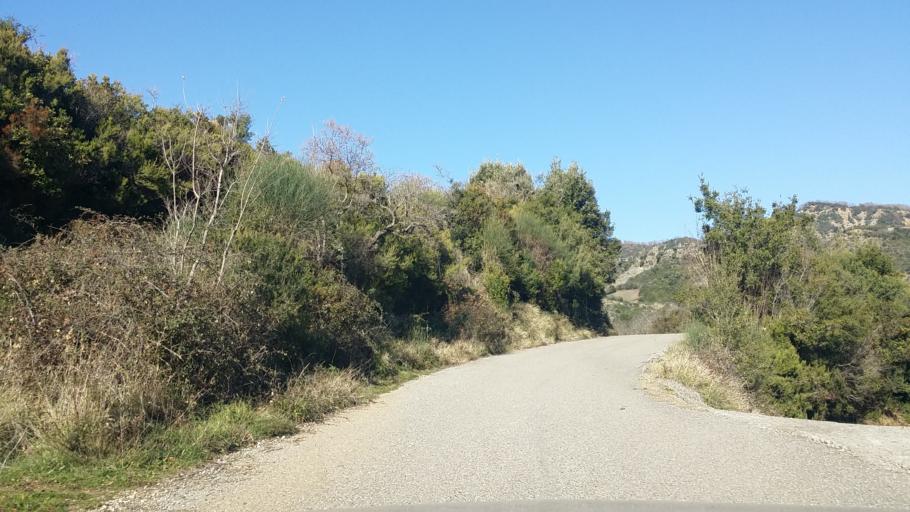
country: GR
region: West Greece
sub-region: Nomos Aitolias kai Akarnanias
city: Krikellos
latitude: 39.0044
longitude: 21.2414
